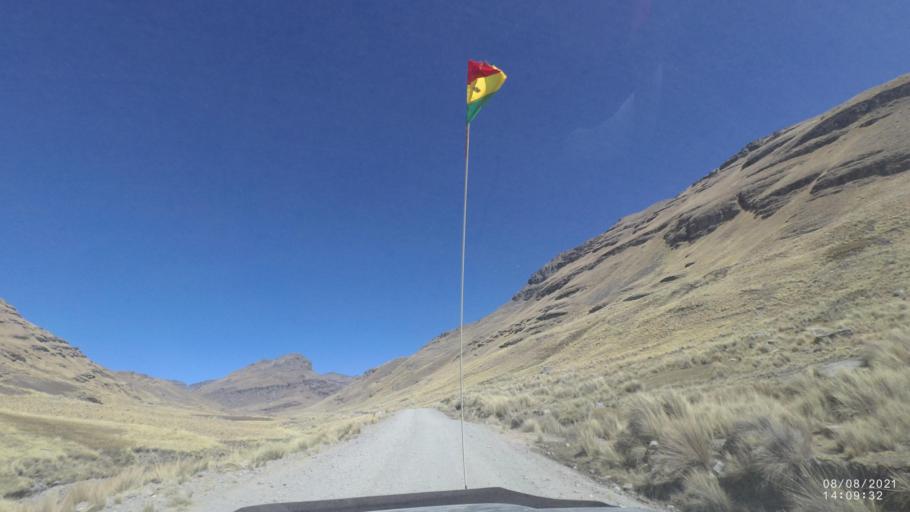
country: BO
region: Cochabamba
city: Sipe Sipe
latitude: -17.1459
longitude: -66.4371
